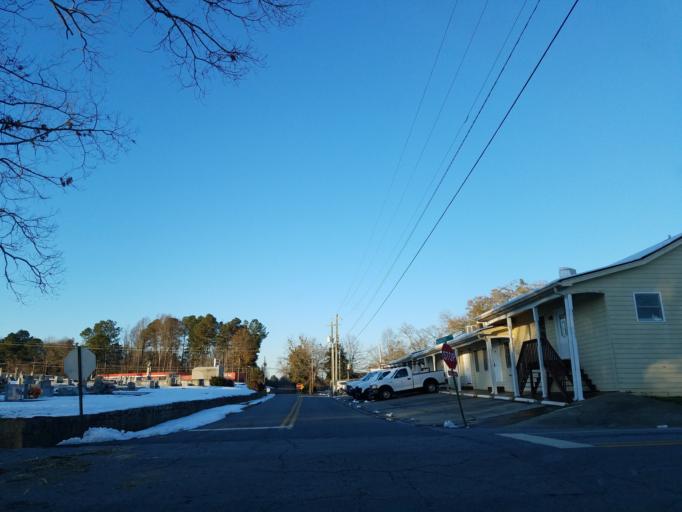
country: US
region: Georgia
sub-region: Dawson County
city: Dawsonville
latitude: 34.4192
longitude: -84.1225
